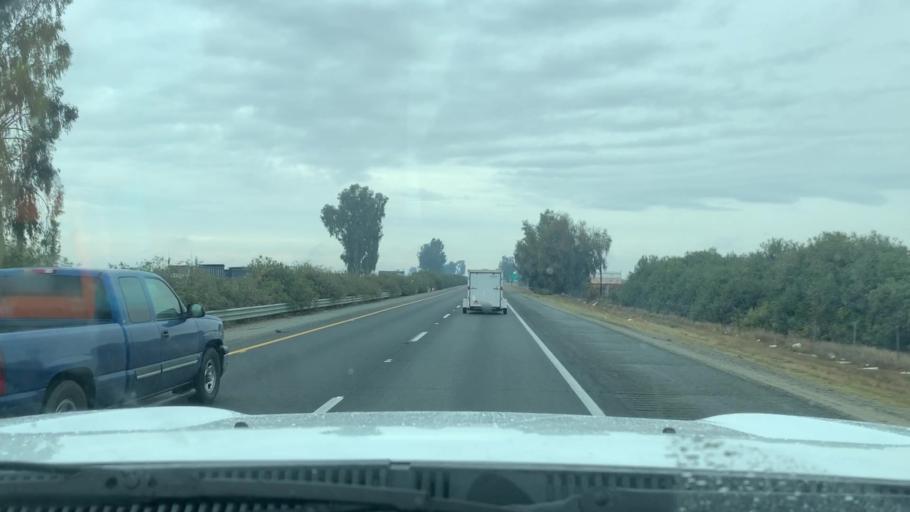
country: US
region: California
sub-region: Tulare County
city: Earlimart
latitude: 35.8272
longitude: -119.2587
